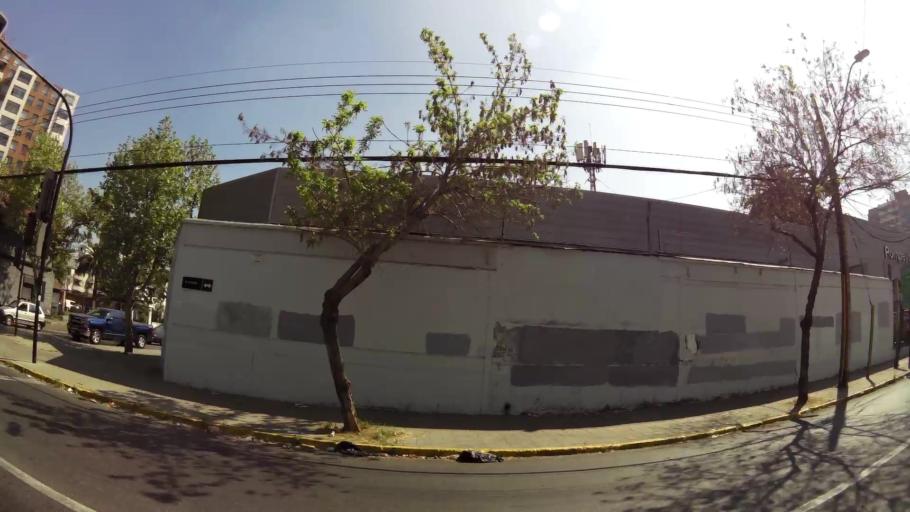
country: CL
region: Santiago Metropolitan
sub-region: Provincia de Santiago
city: Santiago
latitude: -33.4539
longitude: -70.6207
